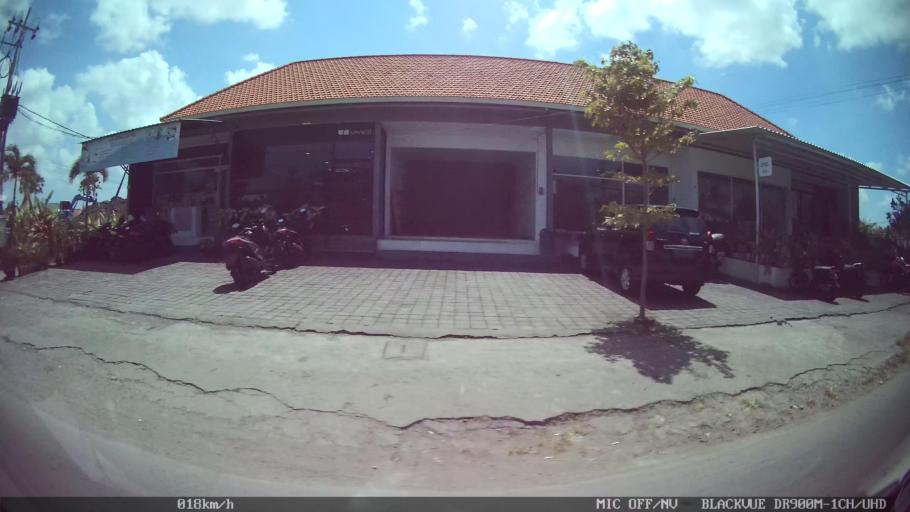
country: ID
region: Bali
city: Banjar Gunungpande
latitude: -8.6659
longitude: 115.1596
